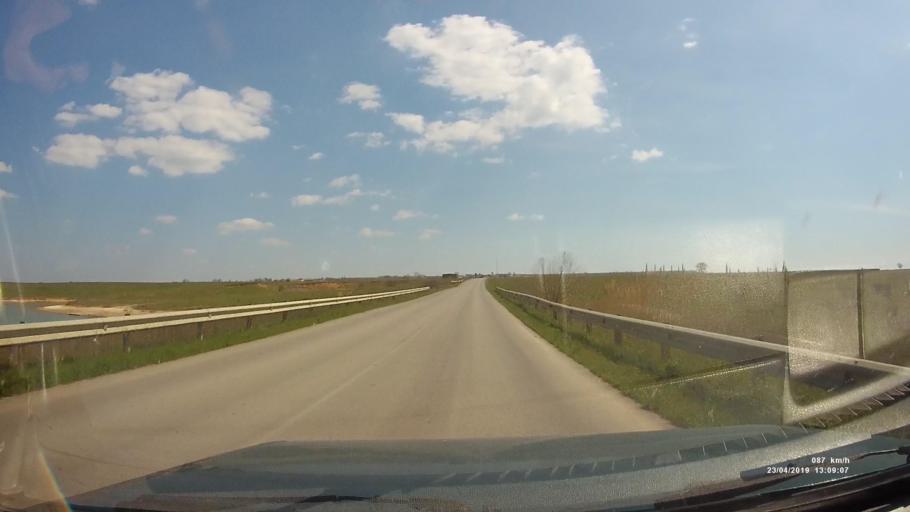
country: RU
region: Kalmykiya
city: Yashalta
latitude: 46.5776
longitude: 42.7854
